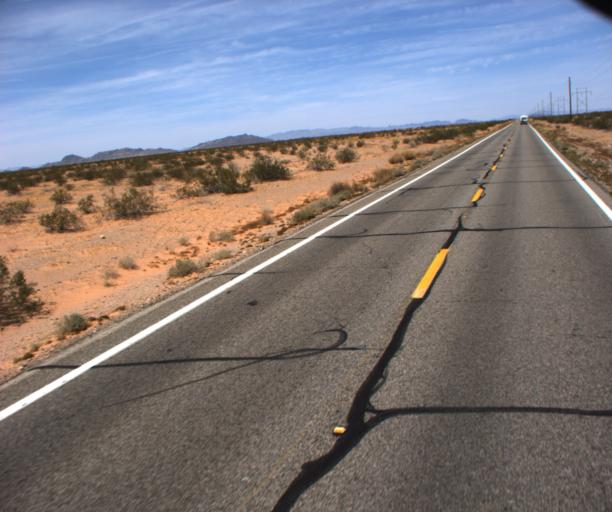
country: US
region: Arizona
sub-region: La Paz County
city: Quartzsite
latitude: 33.8718
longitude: -114.2169
